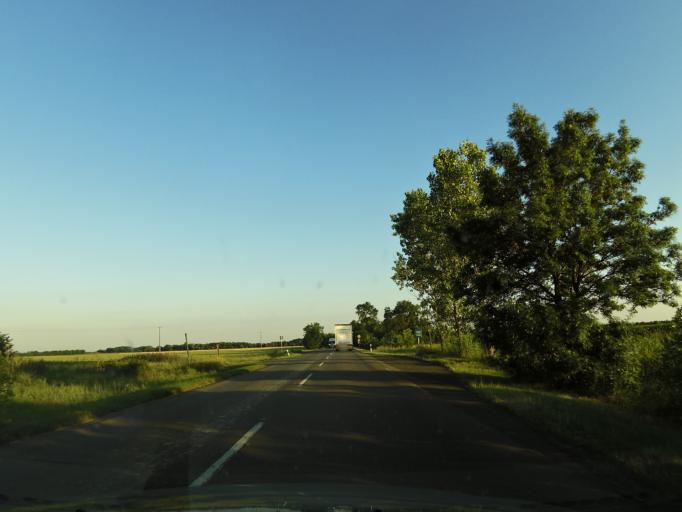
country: HU
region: Csongrad
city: Hodmezovasarhely
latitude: 46.5060
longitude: 20.3141
